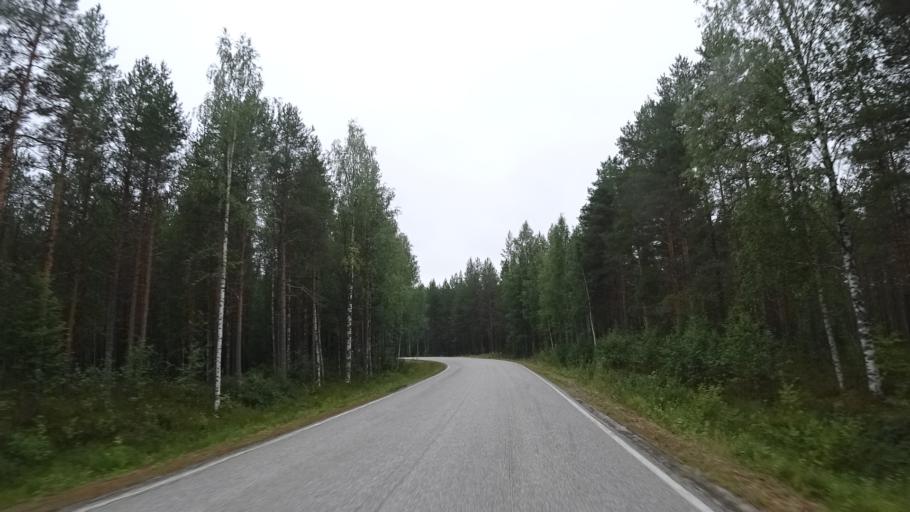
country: FI
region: North Karelia
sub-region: Pielisen Karjala
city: Lieksa
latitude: 63.3285
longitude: 30.2413
